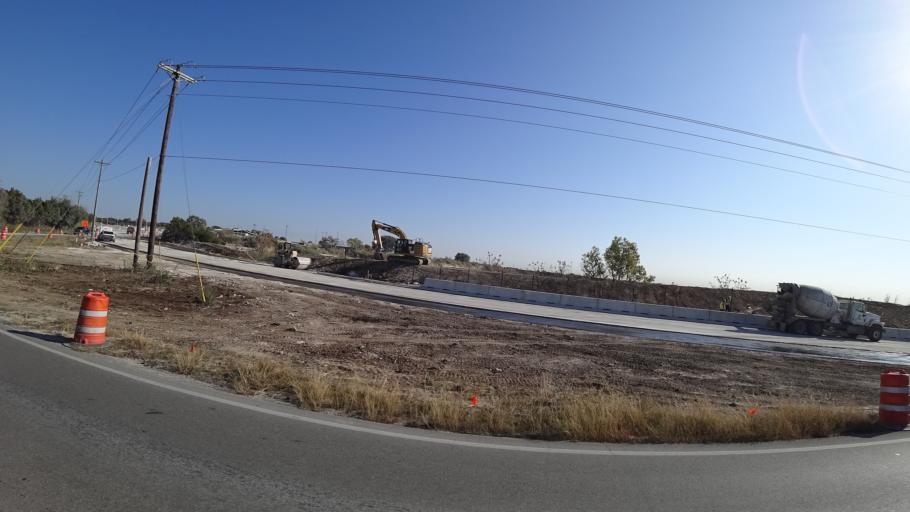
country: US
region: Texas
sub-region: Williamson County
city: Cedar Park
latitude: 30.5009
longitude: -97.8586
